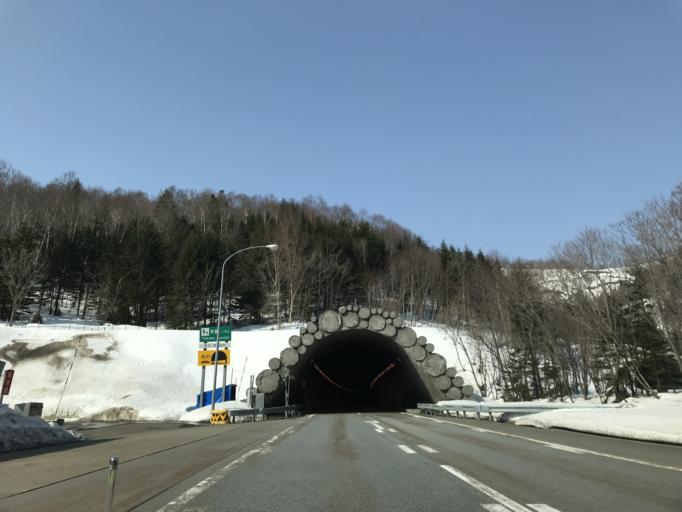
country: JP
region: Hokkaido
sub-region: Asahikawa-shi
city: Asahikawa
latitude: 43.7846
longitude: 142.2357
